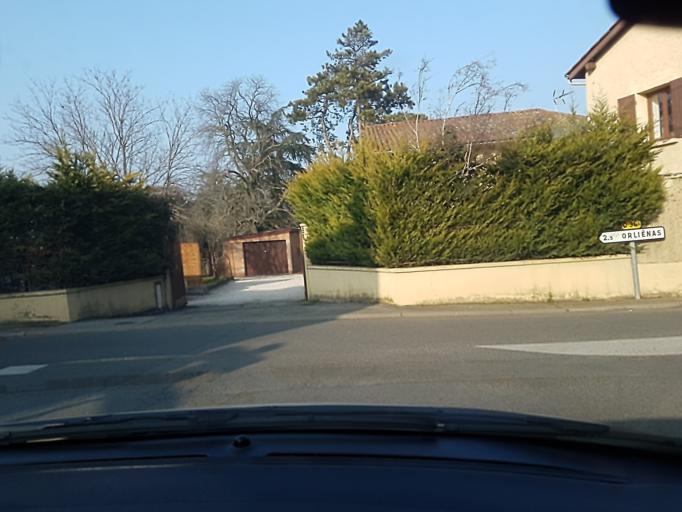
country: FR
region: Rhone-Alpes
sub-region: Departement du Rhone
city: Taluyers
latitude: 45.6409
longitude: 4.7209
